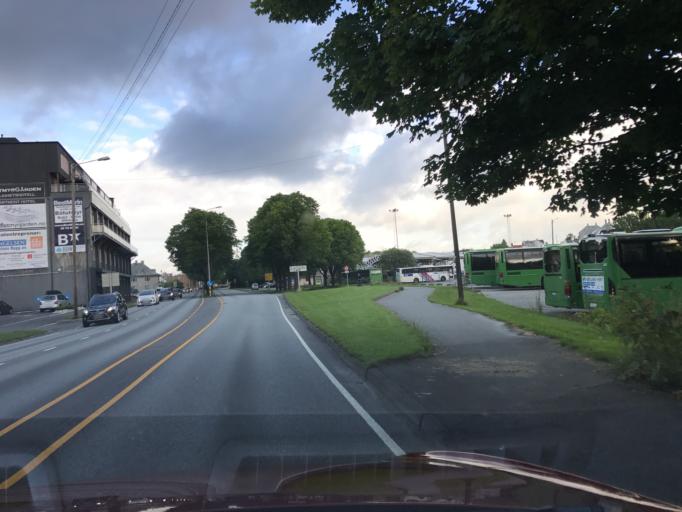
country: NO
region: Rogaland
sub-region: Haugesund
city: Haugesund
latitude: 59.4145
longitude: 5.2757
